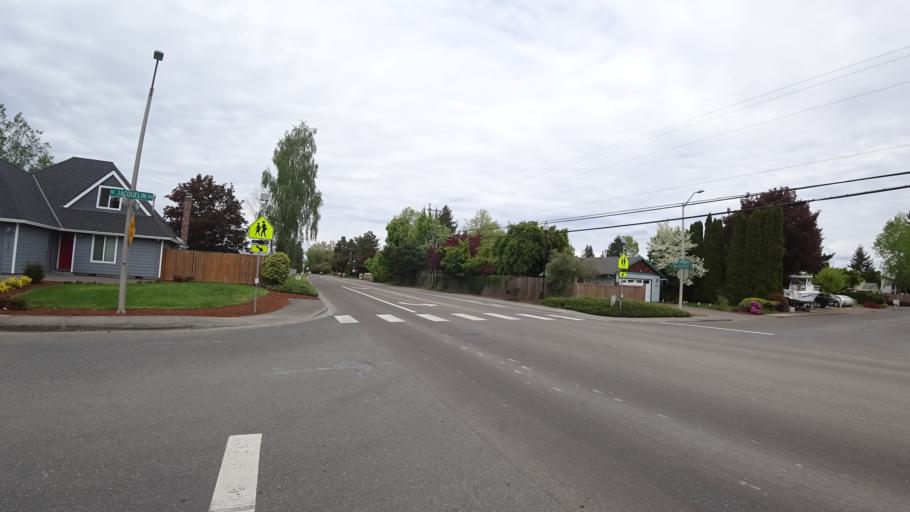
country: US
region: Oregon
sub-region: Washington County
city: Hillsboro
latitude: 45.4982
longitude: -122.9670
